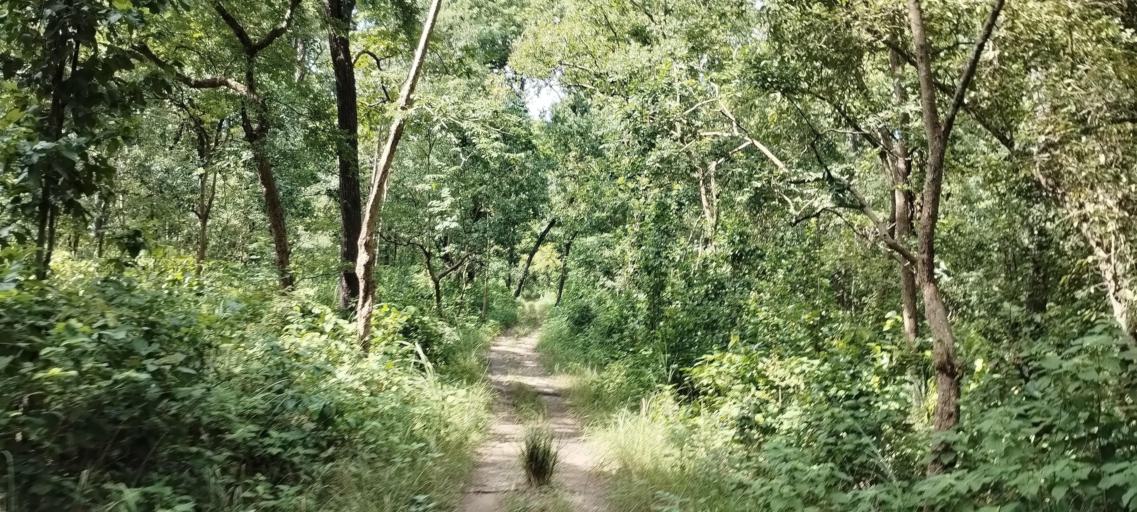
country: NP
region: Far Western
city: Tikapur
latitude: 28.5424
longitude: 81.2867
